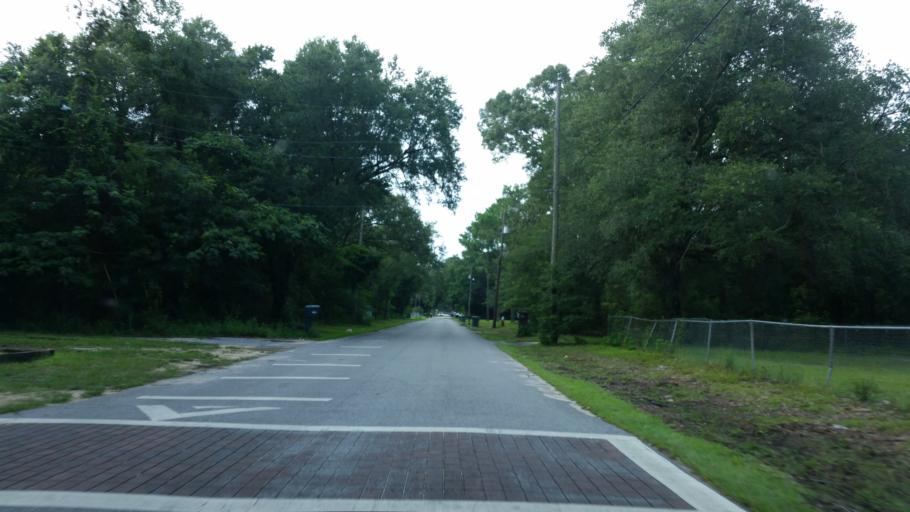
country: US
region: Florida
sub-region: Escambia County
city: Ferry Pass
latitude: 30.5127
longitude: -87.2085
